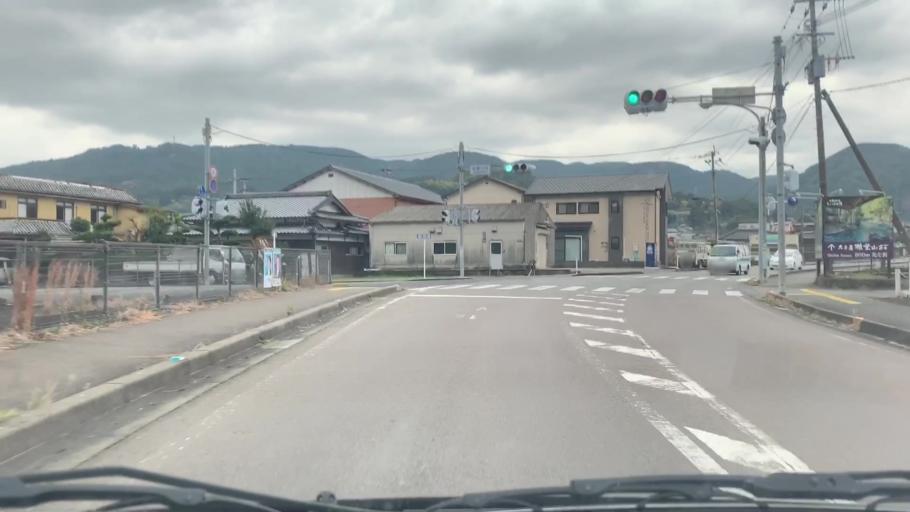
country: JP
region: Saga Prefecture
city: Ureshinomachi-shimojuku
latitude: 33.0914
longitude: 129.9773
